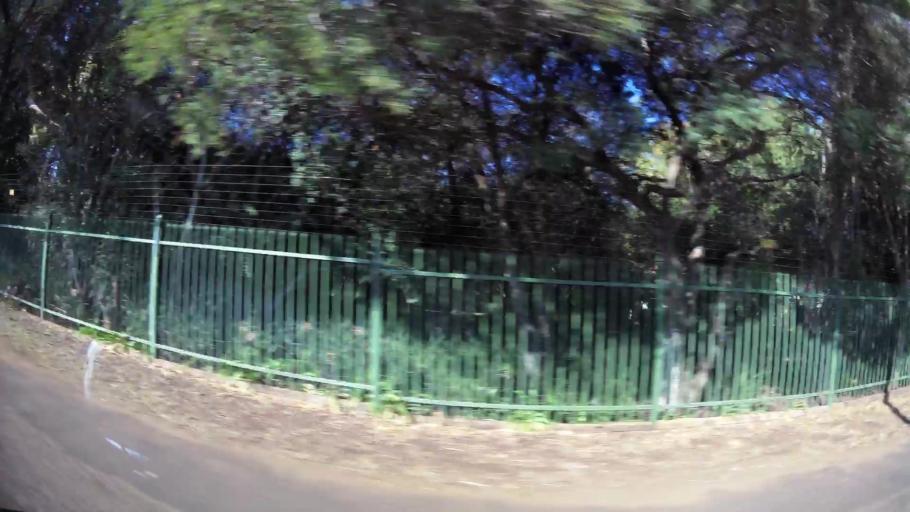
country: ZA
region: Gauteng
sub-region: City of Tshwane Metropolitan Municipality
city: Pretoria
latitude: -25.6479
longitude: 28.2168
